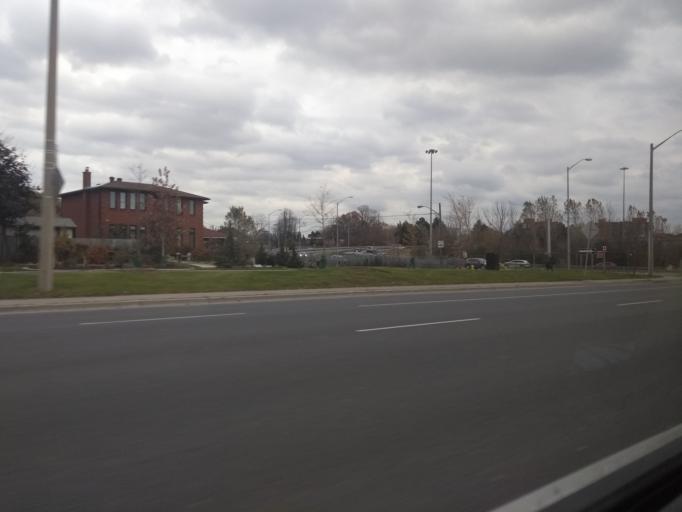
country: CA
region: Ontario
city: Etobicoke
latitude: 43.7132
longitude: -79.5066
